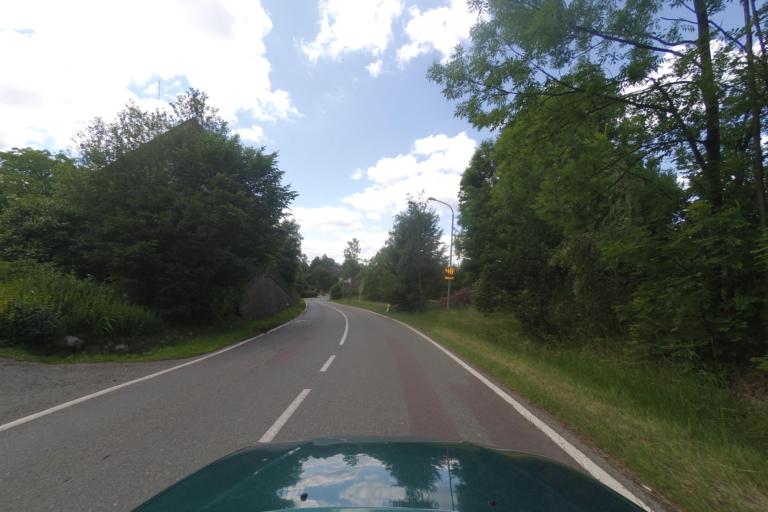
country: CZ
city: Nove Mesto nad Metuji
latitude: 50.3394
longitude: 16.2254
